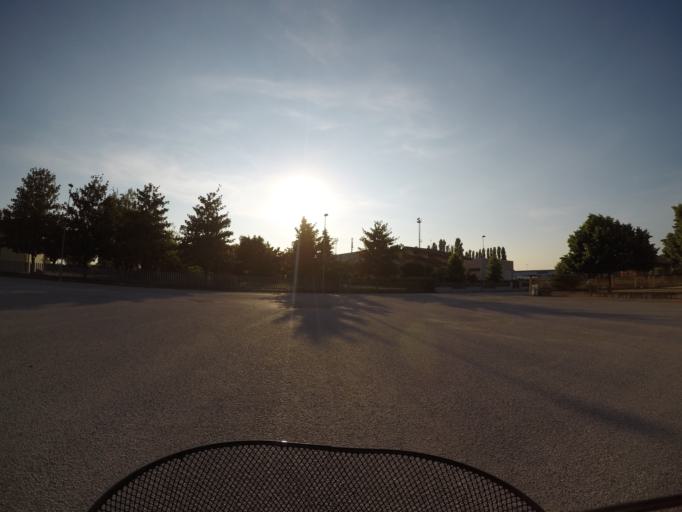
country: IT
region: Veneto
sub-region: Provincia di Rovigo
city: Fratta Polesine
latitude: 45.0275
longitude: 11.6366
